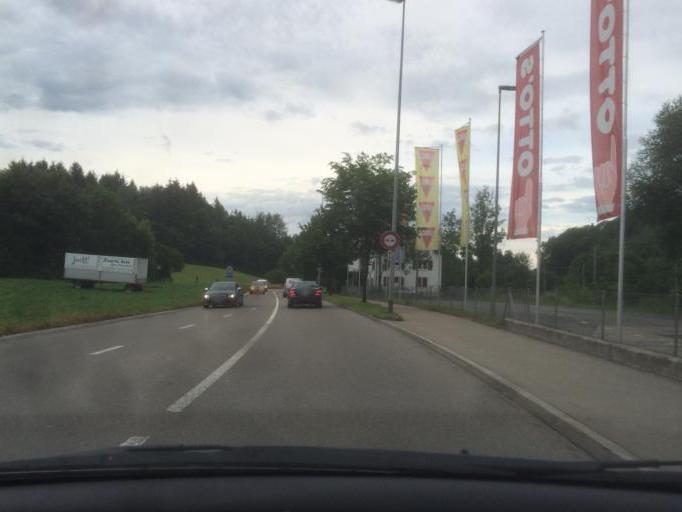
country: CH
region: Zurich
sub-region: Bezirk Hinwil
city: Wetzikon / Robenhausen
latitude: 47.3343
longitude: 8.7715
